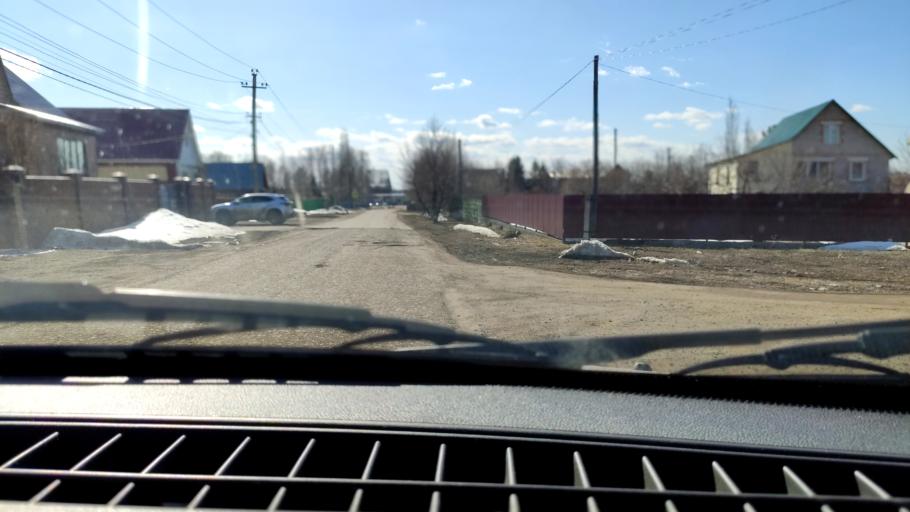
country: RU
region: Bashkortostan
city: Iglino
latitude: 54.8174
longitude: 56.4099
